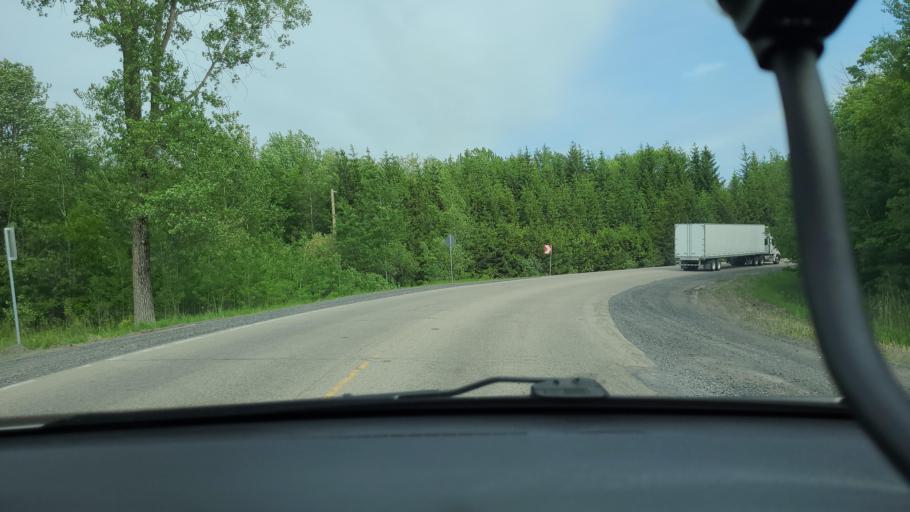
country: CA
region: Quebec
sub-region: Lanaudiere
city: Crabtree
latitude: 45.9693
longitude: -73.4942
